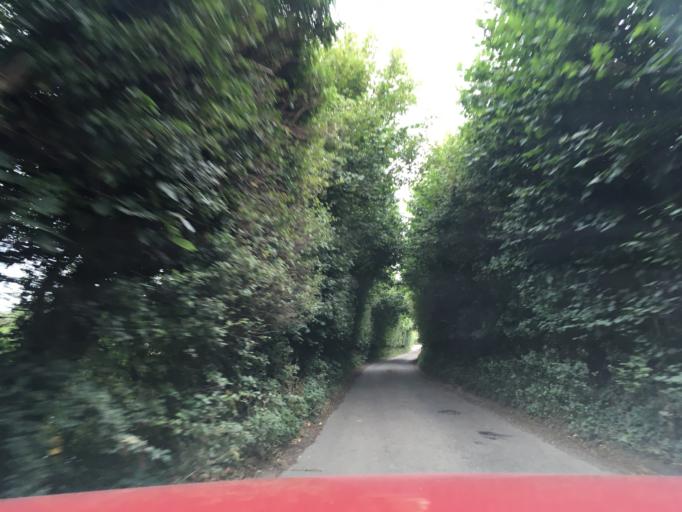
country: GB
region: England
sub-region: Kent
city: Maidstone
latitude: 51.2332
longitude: 0.5412
